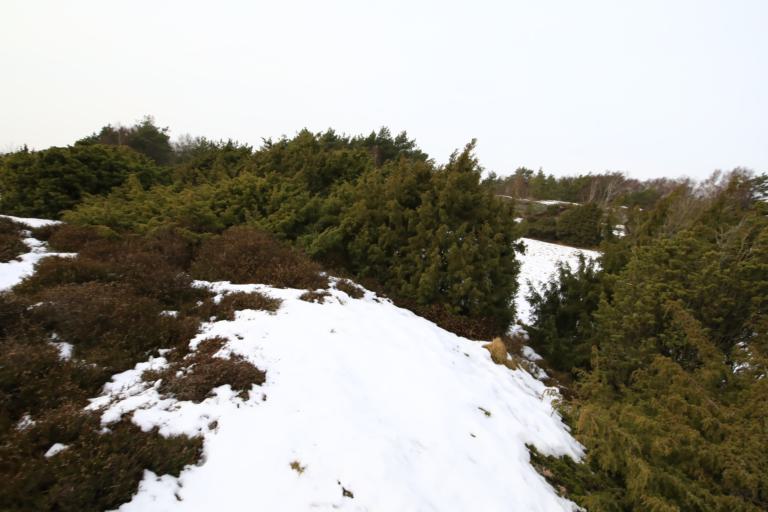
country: SE
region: Halland
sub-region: Kungsbacka Kommun
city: Frillesas
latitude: 57.2186
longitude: 12.1426
